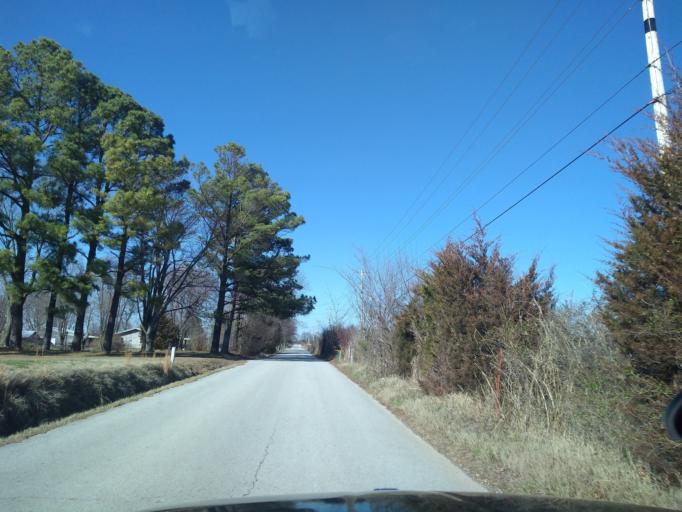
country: US
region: Arkansas
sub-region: Washington County
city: Farmington
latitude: 36.0664
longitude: -94.2400
